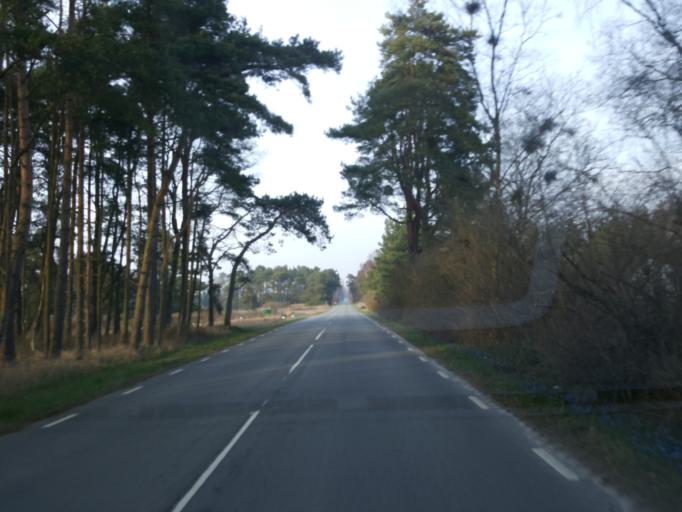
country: SE
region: Skane
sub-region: Simrishamns Kommun
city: Simrishamn
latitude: 55.4165
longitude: 14.2077
